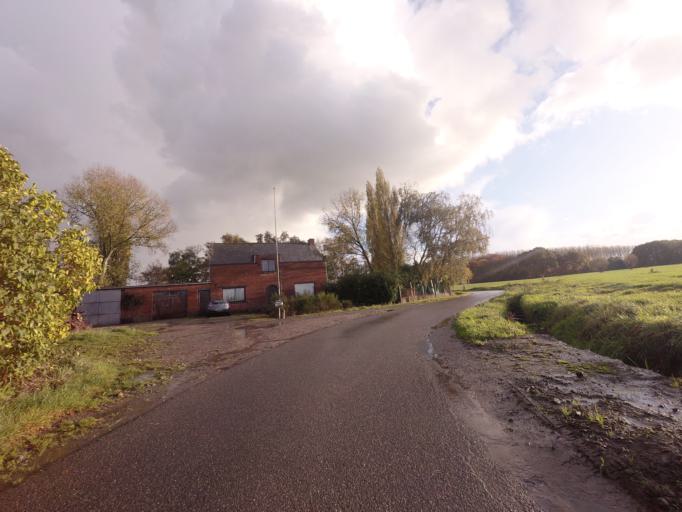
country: BE
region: Flanders
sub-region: Provincie Antwerpen
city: Aartselaar
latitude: 51.1314
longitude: 4.3650
